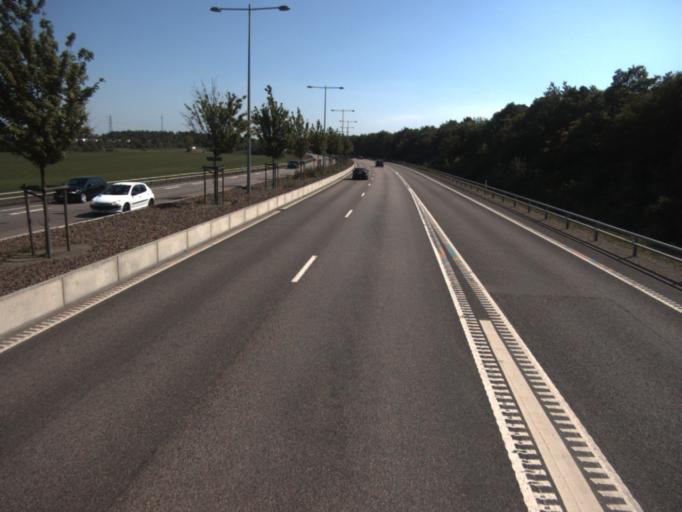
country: SE
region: Skane
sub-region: Helsingborg
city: Gantofta
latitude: 56.0250
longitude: 12.7606
